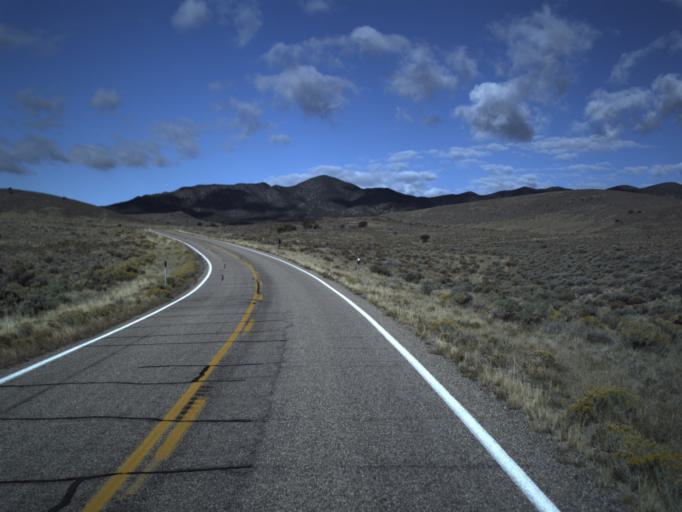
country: US
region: Utah
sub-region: Beaver County
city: Milford
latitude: 38.4568
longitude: -113.2197
